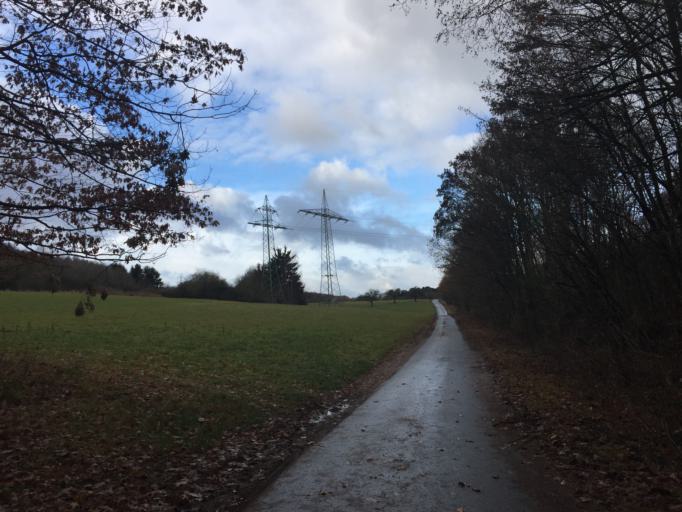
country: DE
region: Hesse
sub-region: Regierungsbezirk Giessen
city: Lich
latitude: 50.5433
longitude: 8.7886
